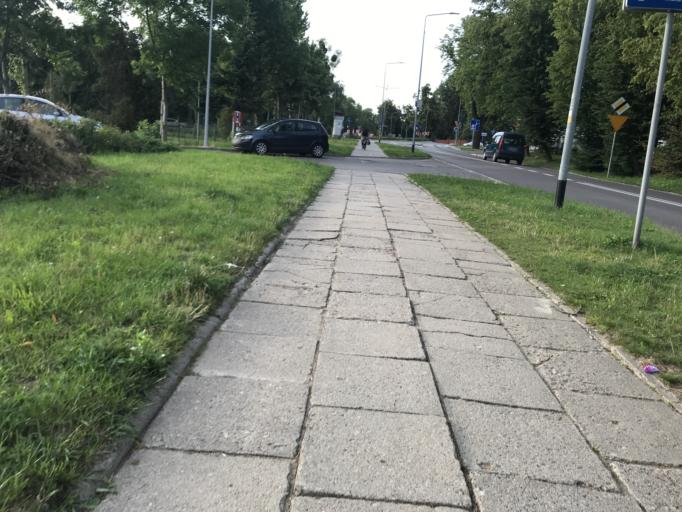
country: PL
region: Warmian-Masurian Voivodeship
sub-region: Powiat elblaski
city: Elblag
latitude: 54.1665
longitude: 19.4245
